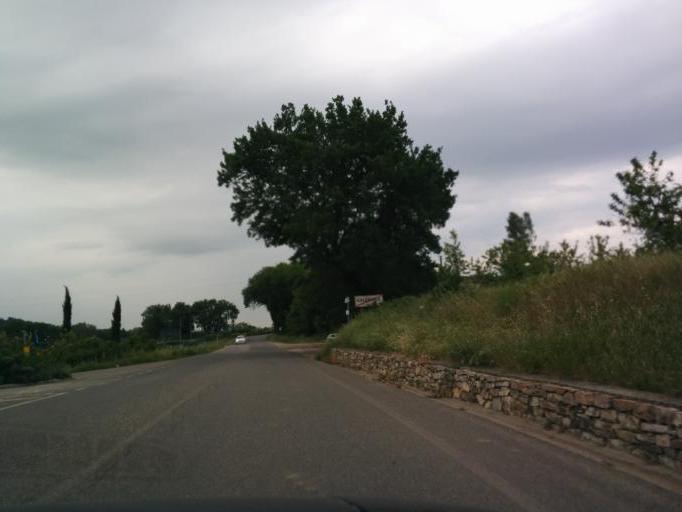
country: IT
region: Tuscany
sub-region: Province of Florence
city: San Casciano in Val di Pesa
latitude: 43.6389
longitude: 11.1732
